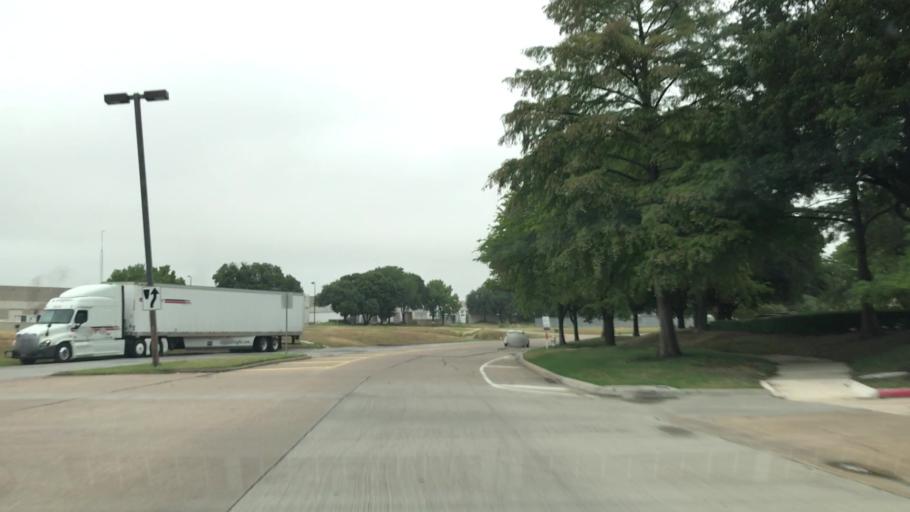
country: US
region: Texas
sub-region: Dallas County
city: Coppell
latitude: 32.9246
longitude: -97.0194
